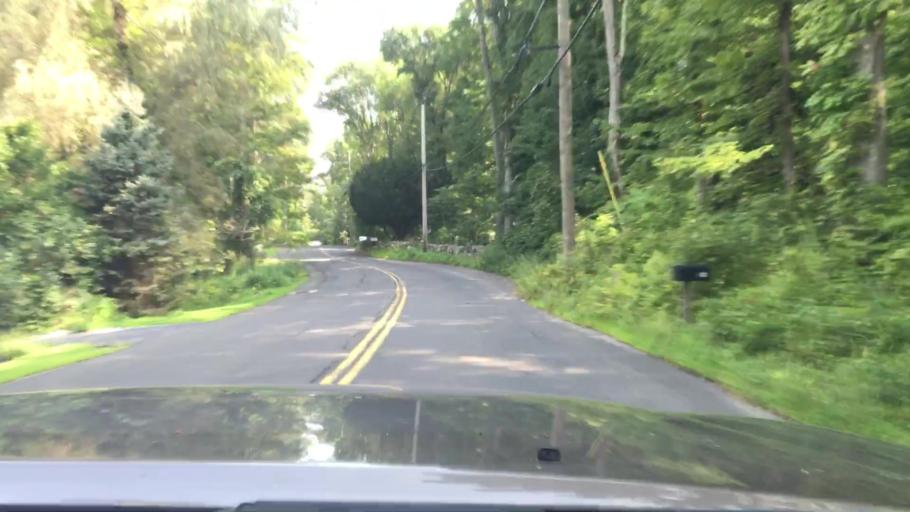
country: US
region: Connecticut
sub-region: Fairfield County
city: Georgetown
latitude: 41.2436
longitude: -73.4561
